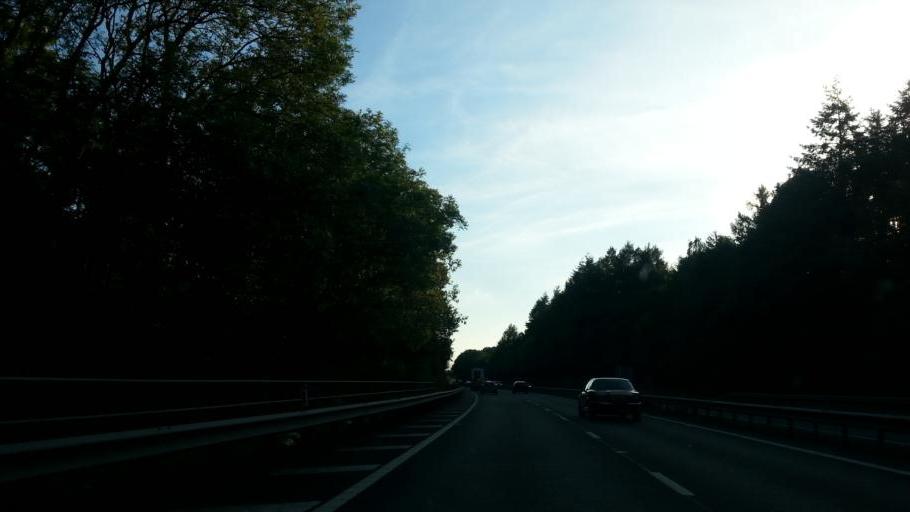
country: GB
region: England
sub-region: Herefordshire
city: Linton
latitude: 51.9390
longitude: -2.4763
